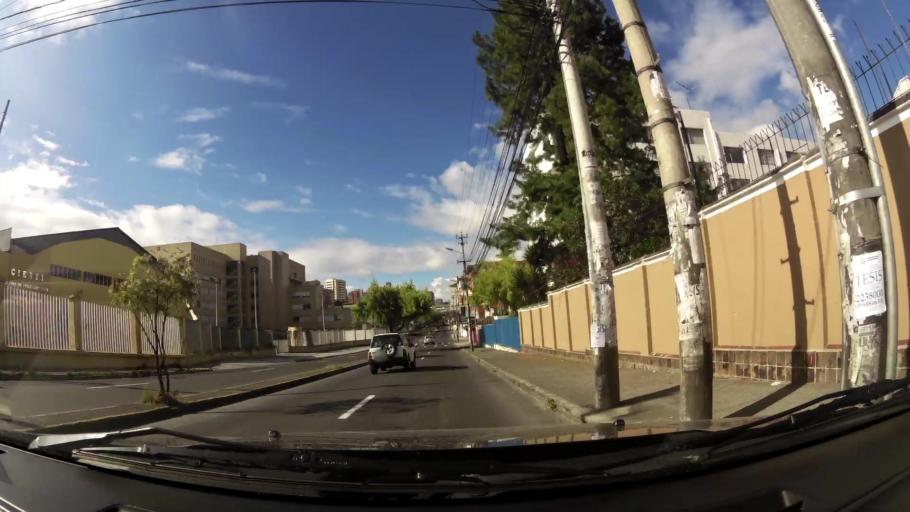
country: EC
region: Pichincha
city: Quito
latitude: -0.2105
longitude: -78.4873
